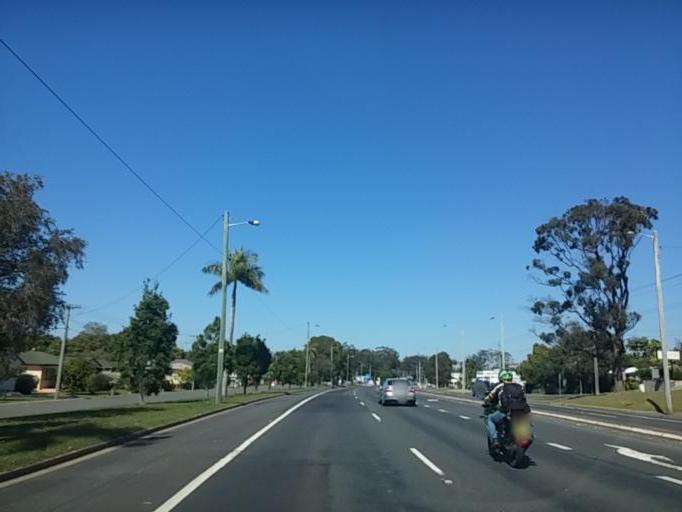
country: AU
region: New South Wales
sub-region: Coffs Harbour
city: Coffs Harbour
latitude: -30.2877
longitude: 153.1237
